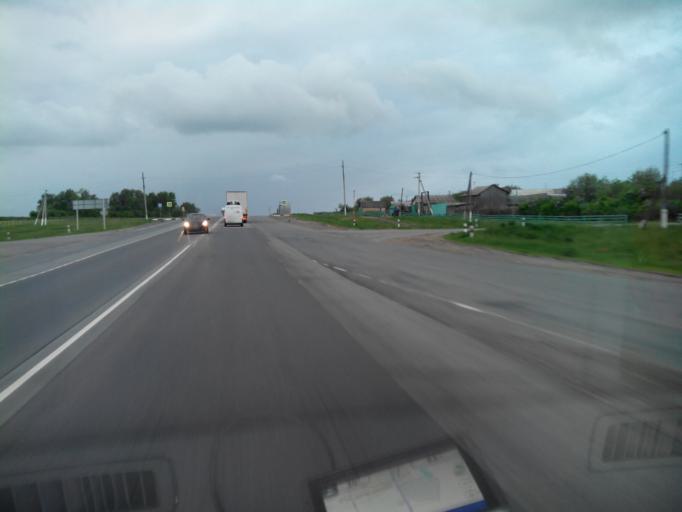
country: RU
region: Penza
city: Chemodanovka
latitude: 53.2347
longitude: 45.3800
